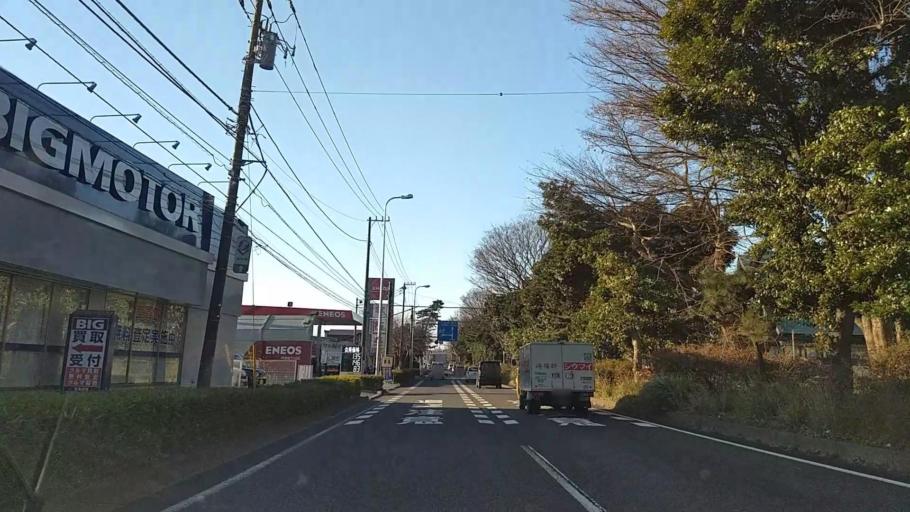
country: JP
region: Kanagawa
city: Fujisawa
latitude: 35.3726
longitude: 139.5024
